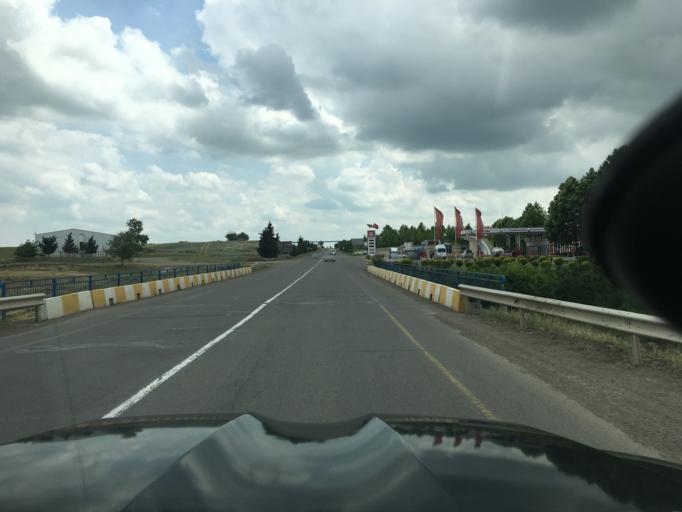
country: AZ
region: Tovuz
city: Tovuz
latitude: 40.9754
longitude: 45.6743
